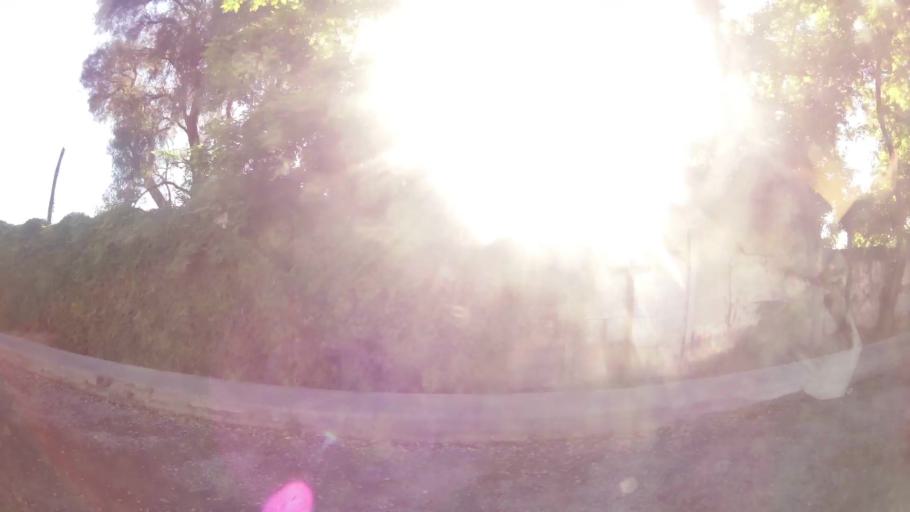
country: CL
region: Santiago Metropolitan
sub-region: Provincia de Maipo
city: San Bernardo
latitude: -33.6406
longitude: -70.6912
